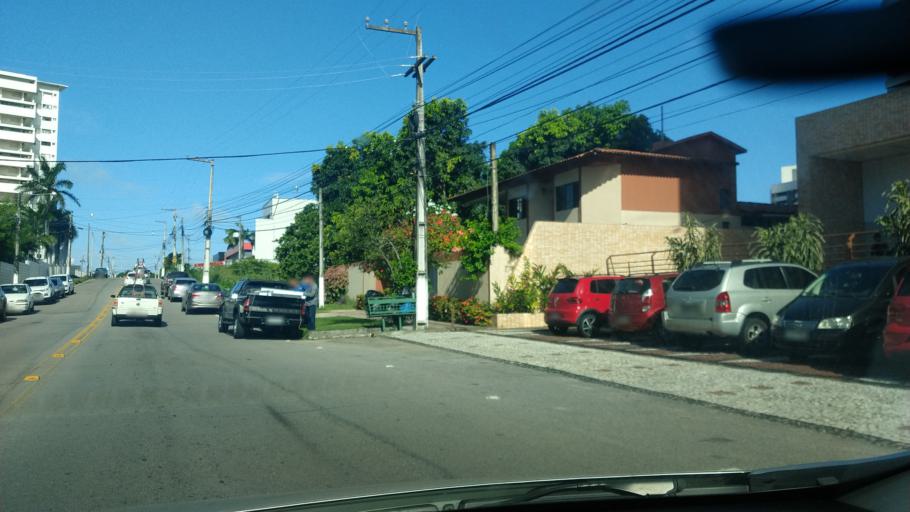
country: BR
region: Rio Grande do Norte
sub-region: Natal
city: Natal
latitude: -5.8331
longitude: -35.2144
